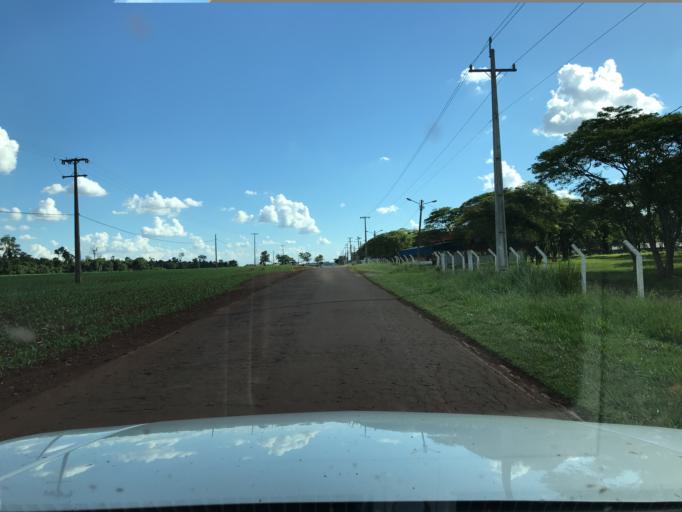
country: BR
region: Parana
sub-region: Palotina
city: Palotina
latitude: -24.2702
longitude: -53.8063
